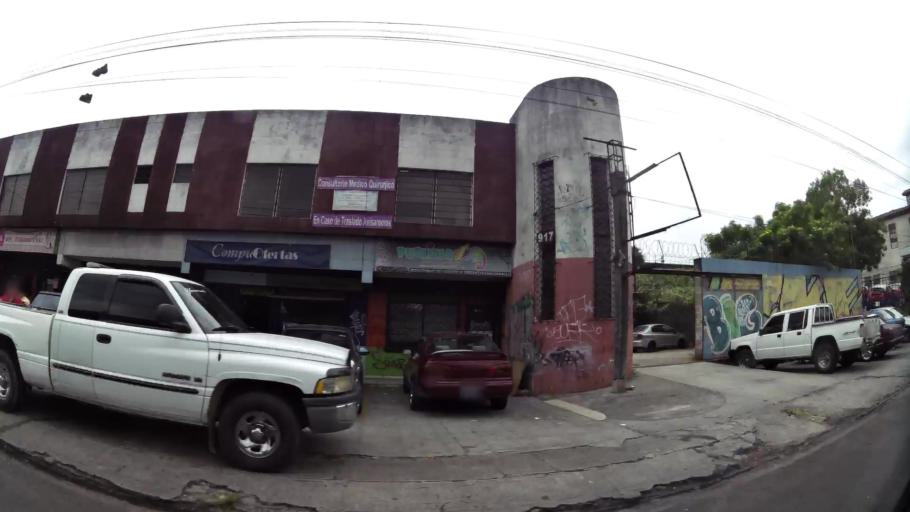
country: SV
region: San Salvador
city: San Salvador
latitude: 13.7008
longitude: -89.1990
